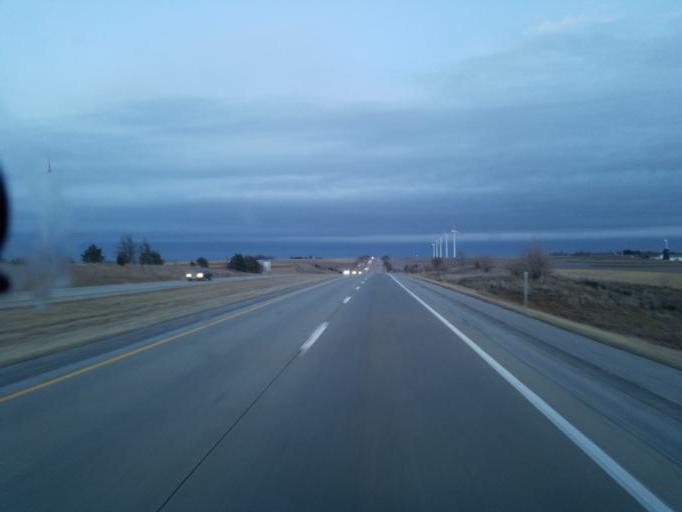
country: US
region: Iowa
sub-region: Pottawattamie County
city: Avoca
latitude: 41.4972
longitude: -95.2015
